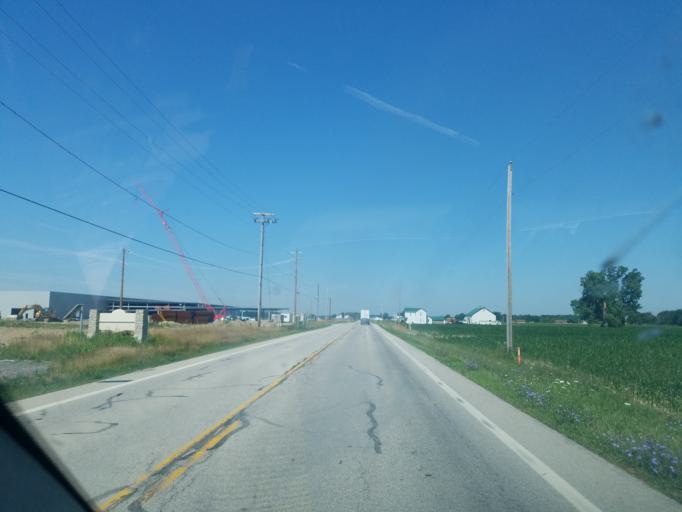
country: US
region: Ohio
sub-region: Shelby County
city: Jackson Center
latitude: 40.4397
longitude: -84.0586
